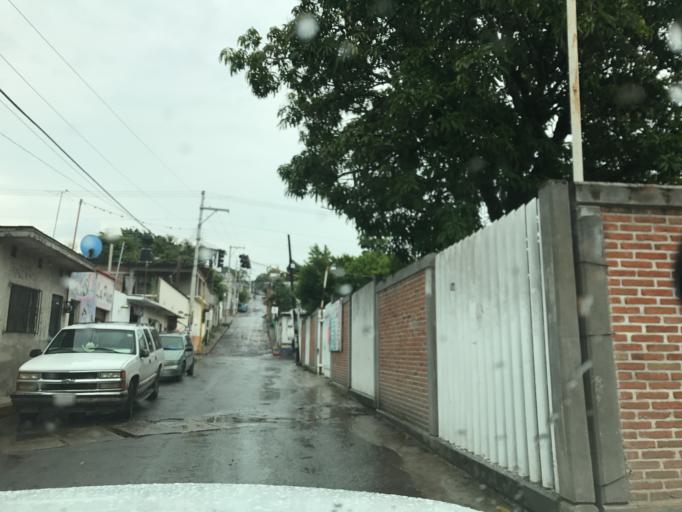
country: MX
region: Morelos
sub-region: Ayala
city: Ciudad Ayala
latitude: 18.7627
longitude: -98.9845
